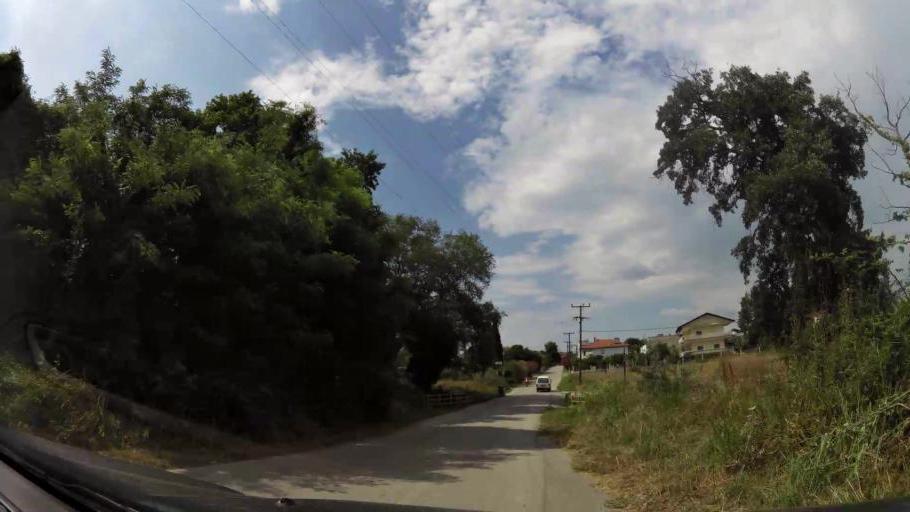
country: GR
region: Central Macedonia
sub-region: Nomos Pierias
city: Makrygialos
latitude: 40.4103
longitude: 22.6076
